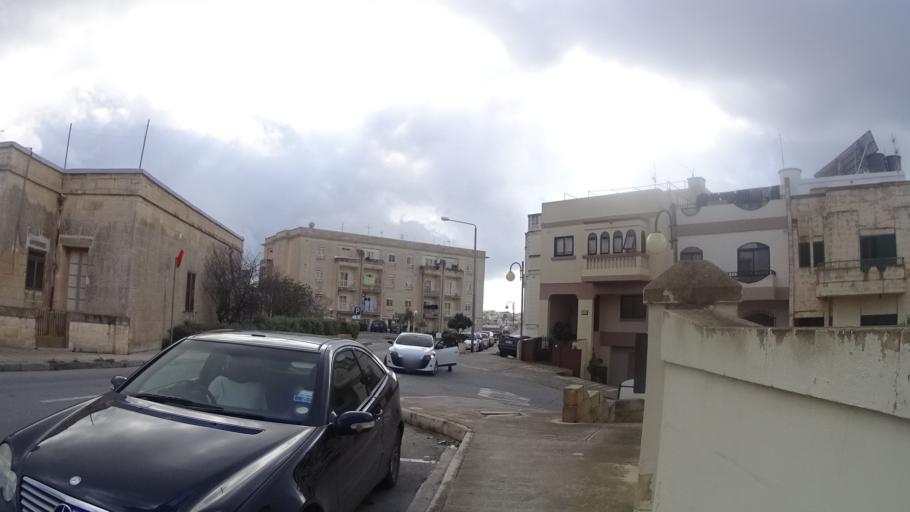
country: MT
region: L-Imtarfa
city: Imtarfa
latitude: 35.8920
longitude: 14.3981
